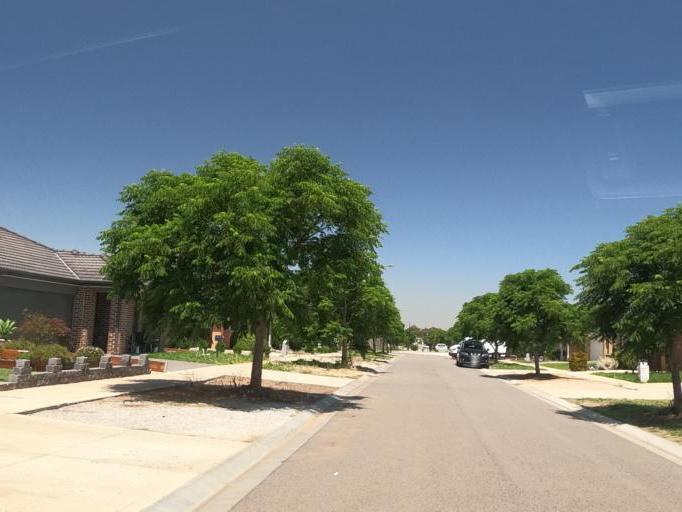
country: AU
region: Victoria
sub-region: Hume
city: Greenvale
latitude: -37.6233
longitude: 144.8755
